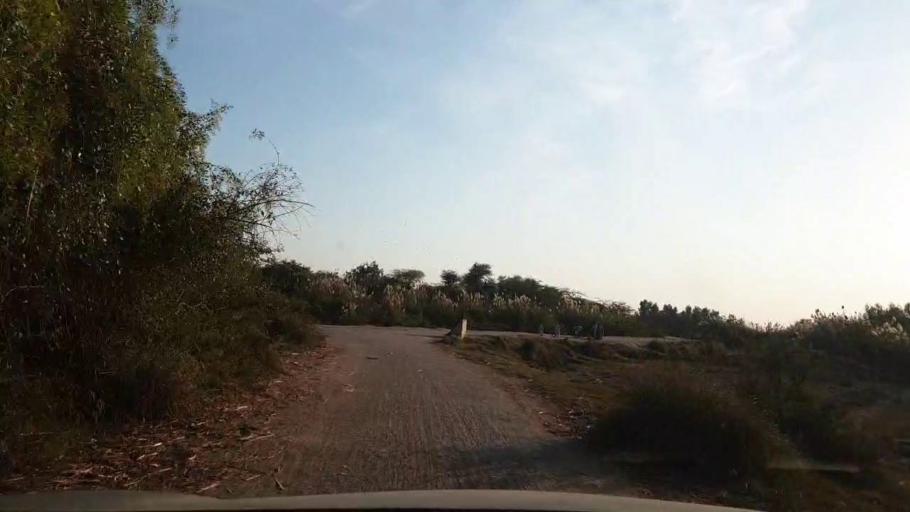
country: PK
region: Sindh
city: Tando Adam
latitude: 25.6170
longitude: 68.6712
